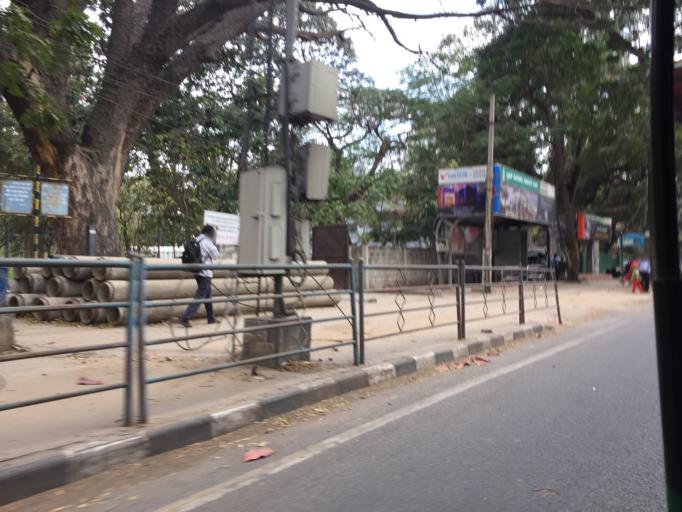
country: IN
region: Karnataka
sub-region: Bangalore Urban
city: Bangalore
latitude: 12.9724
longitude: 77.6107
